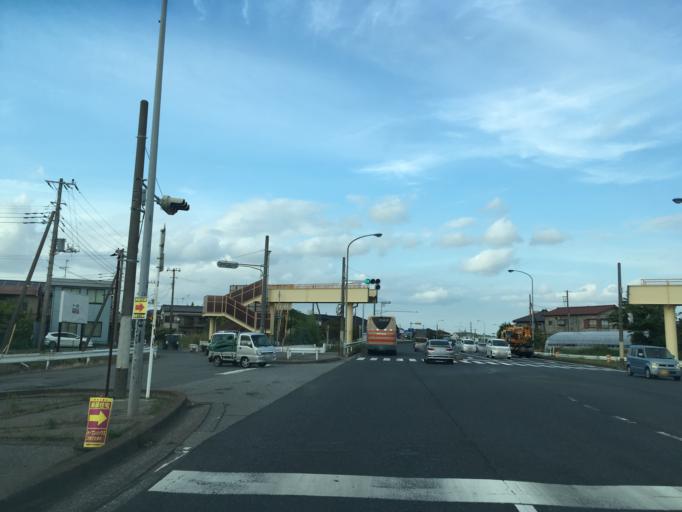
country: JP
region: Chiba
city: Kisarazu
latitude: 35.4064
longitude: 139.9448
